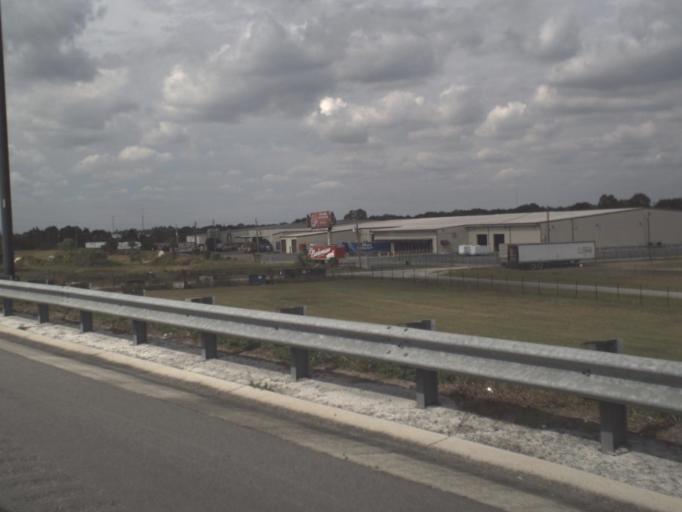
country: US
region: Florida
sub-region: Polk County
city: Crystal Lake
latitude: 28.0089
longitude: -81.8771
